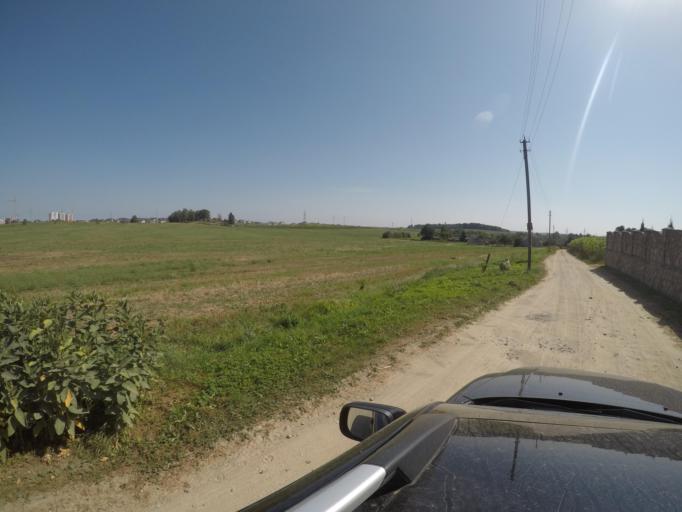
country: BY
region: Grodnenskaya
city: Hrodna
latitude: 53.7092
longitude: 23.8736
